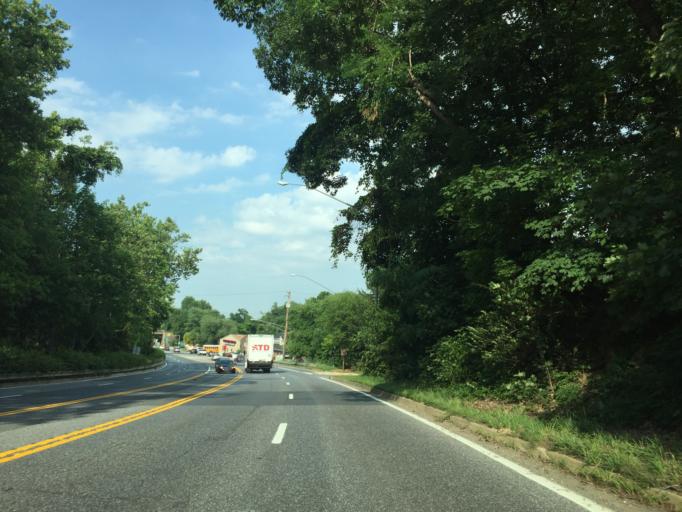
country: US
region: Maryland
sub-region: Howard County
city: Elkridge
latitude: 39.2146
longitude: -76.7145
